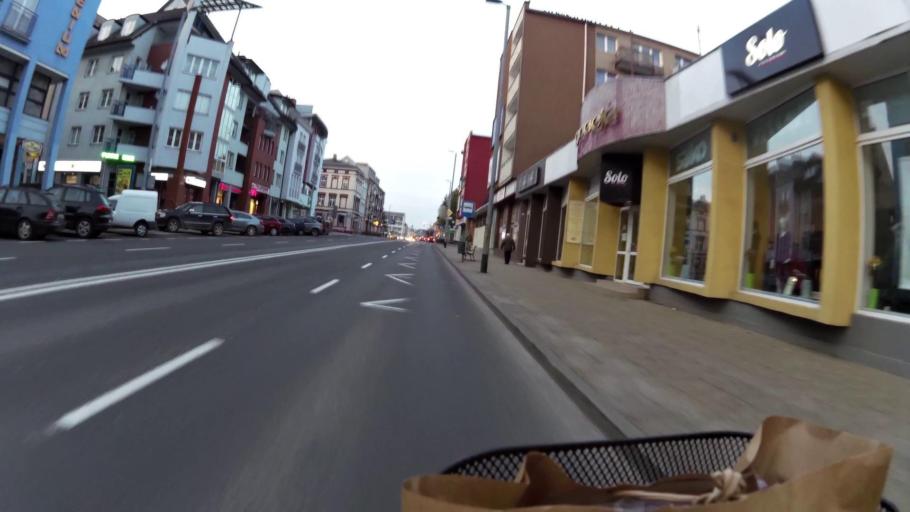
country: PL
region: West Pomeranian Voivodeship
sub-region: Koszalin
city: Koszalin
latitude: 54.1885
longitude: 16.1828
